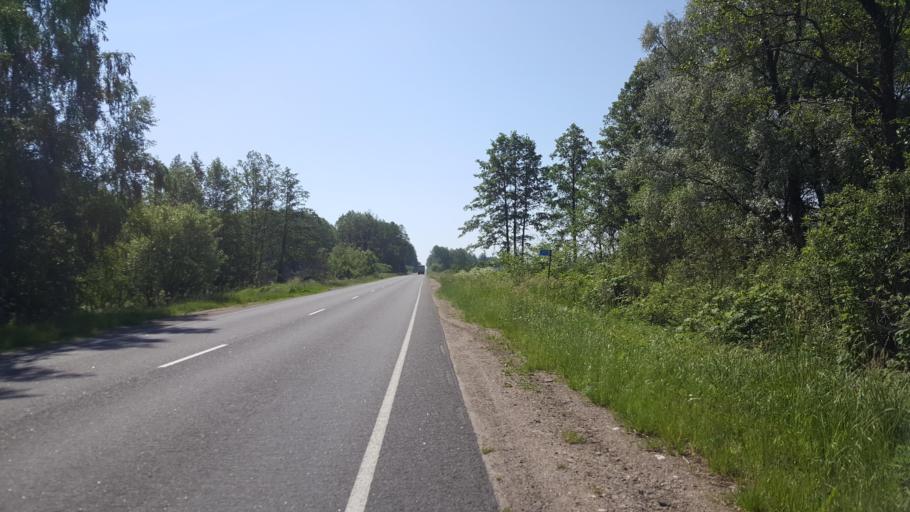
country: BY
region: Brest
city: Zhabinka
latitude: 52.2755
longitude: 23.9520
